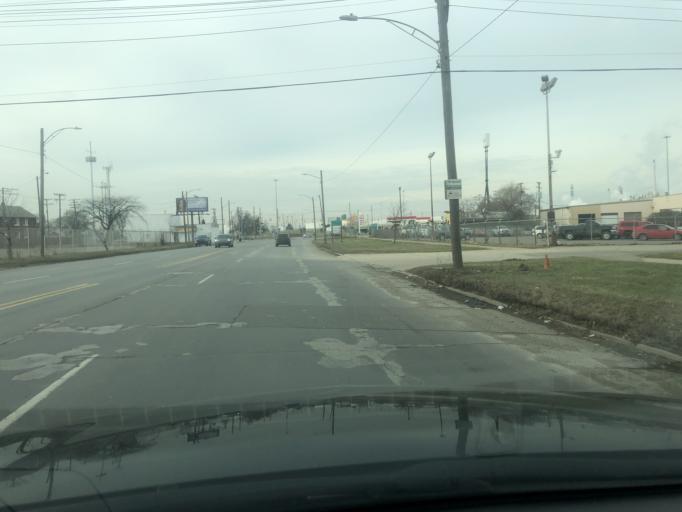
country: US
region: Michigan
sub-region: Wayne County
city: River Rouge
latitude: 42.2755
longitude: -83.1531
